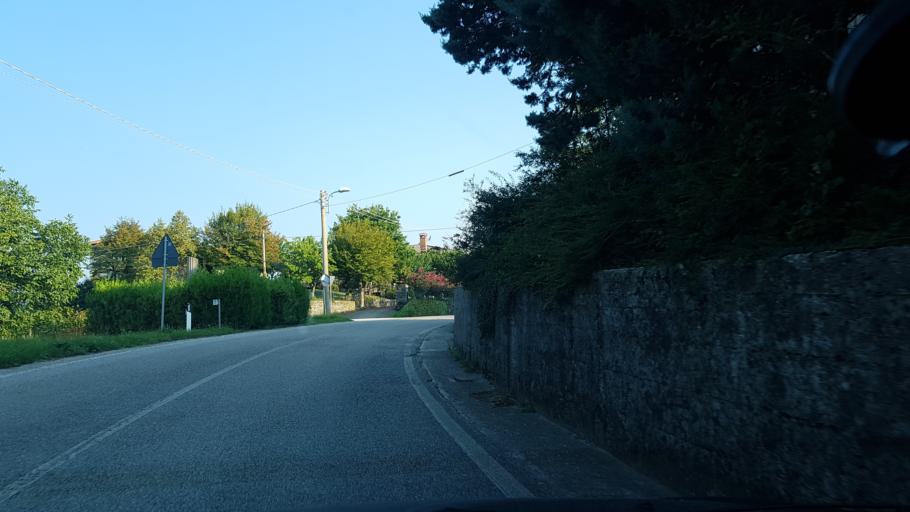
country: IT
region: Friuli Venezia Giulia
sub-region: Provincia di Gorizia
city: San Floriano del Collio
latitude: 45.9818
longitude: 13.6089
